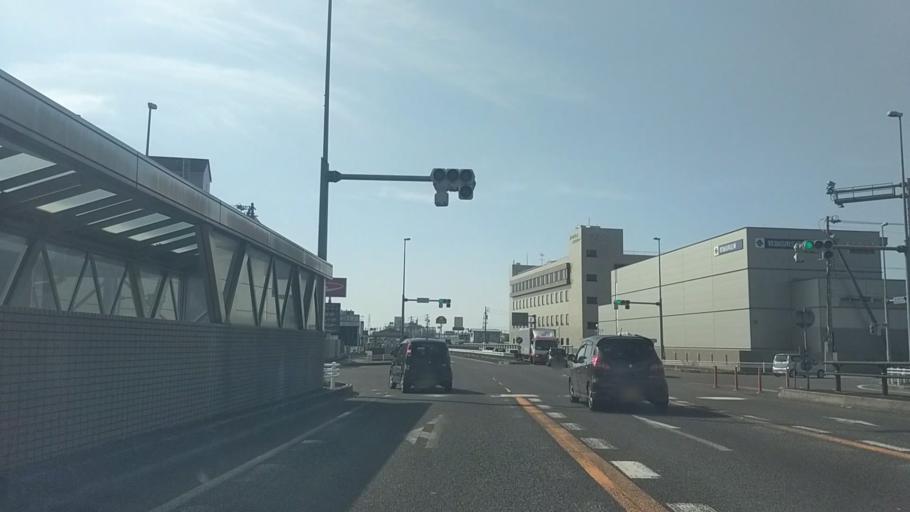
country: JP
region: Aichi
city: Anjo
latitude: 34.9924
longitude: 137.0793
